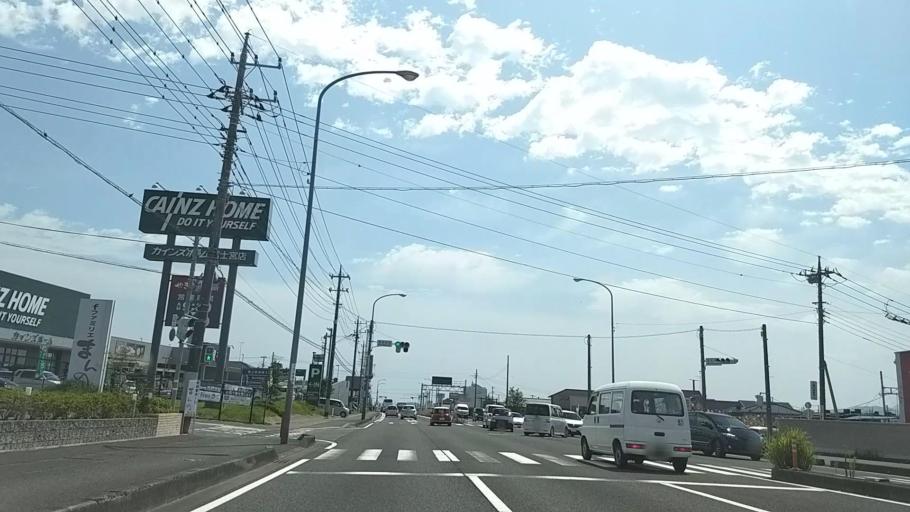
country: JP
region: Shizuoka
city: Fujinomiya
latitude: 35.2559
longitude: 138.6156
